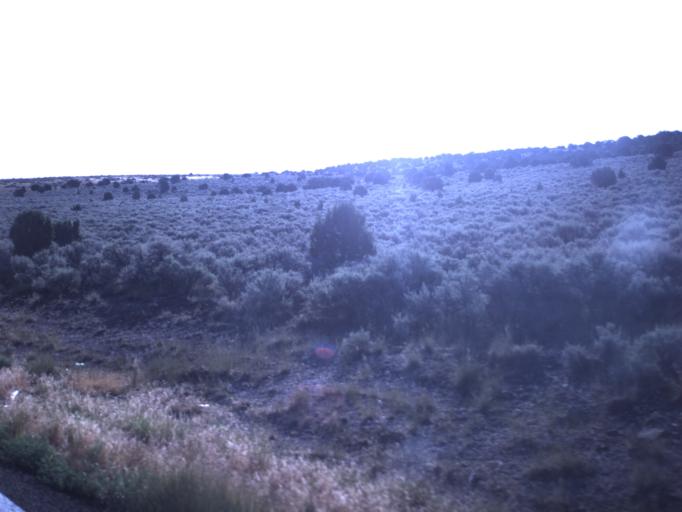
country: US
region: Utah
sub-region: Iron County
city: Parowan
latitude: 38.0559
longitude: -112.9698
